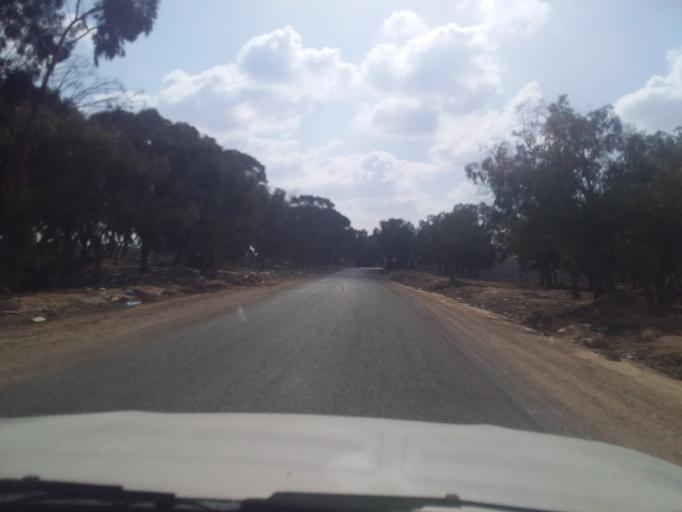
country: TN
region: Qabis
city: Gabes
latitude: 33.6261
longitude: 10.2738
